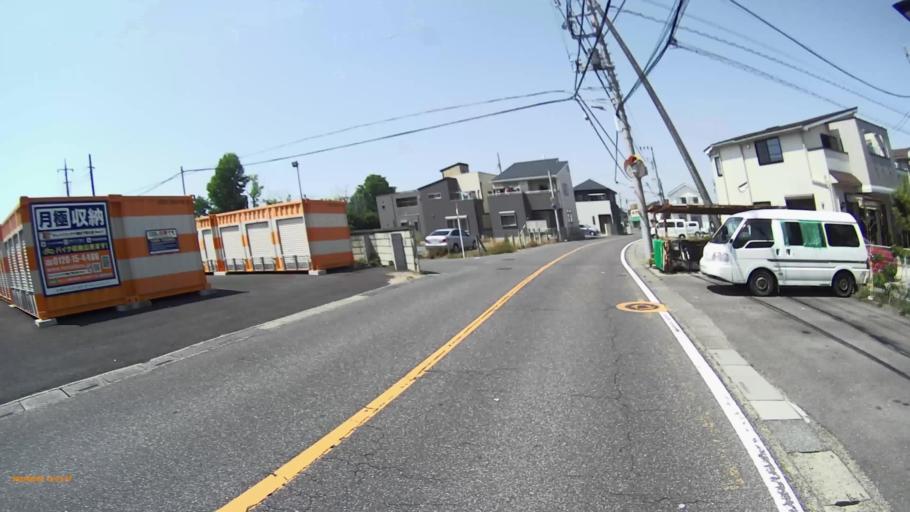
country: JP
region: Saitama
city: Koshigaya
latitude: 35.9284
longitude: 139.7803
